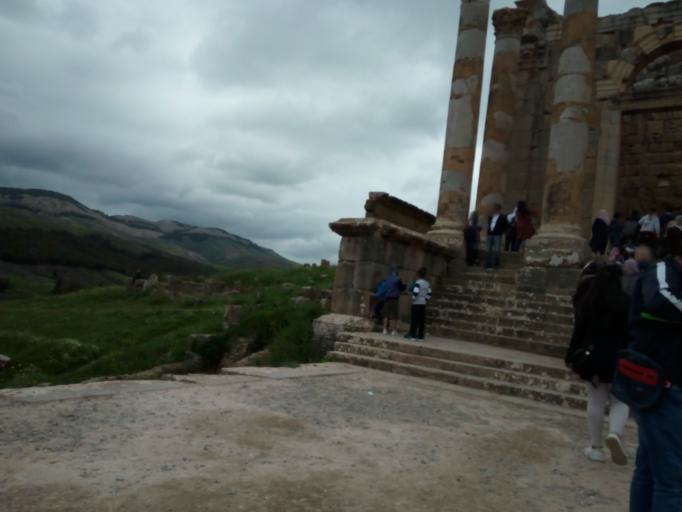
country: DZ
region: Setif
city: El Eulma
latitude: 36.3208
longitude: 5.7362
